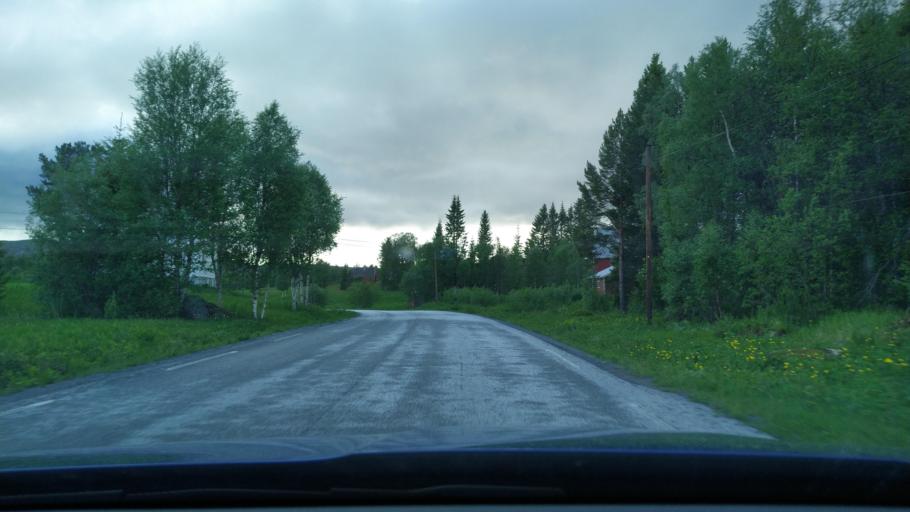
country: NO
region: Troms
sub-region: Dyroy
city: Brostadbotn
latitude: 69.0550
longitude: 17.7986
